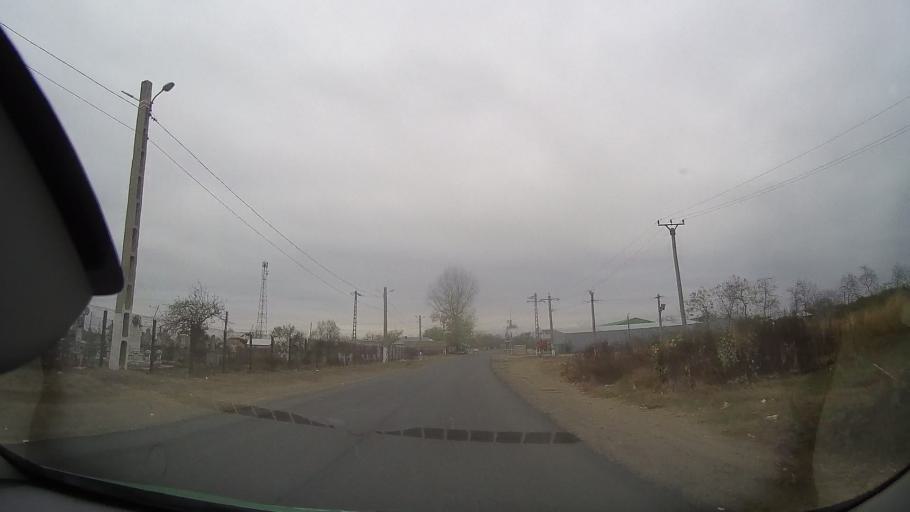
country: RO
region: Braila
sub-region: Comuna Ciresu
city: Ciresu
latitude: 44.9440
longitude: 27.3340
